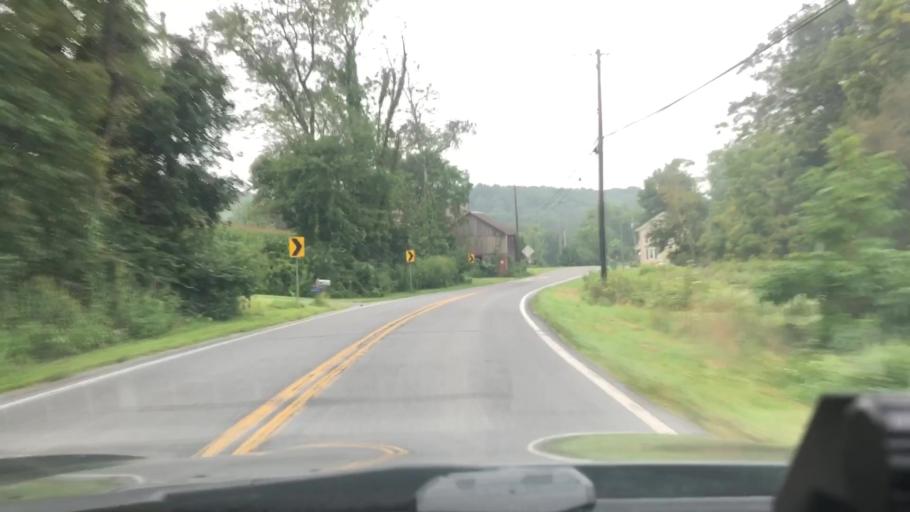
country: US
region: Pennsylvania
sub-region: Berks County
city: Kutztown
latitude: 40.5719
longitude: -75.8059
